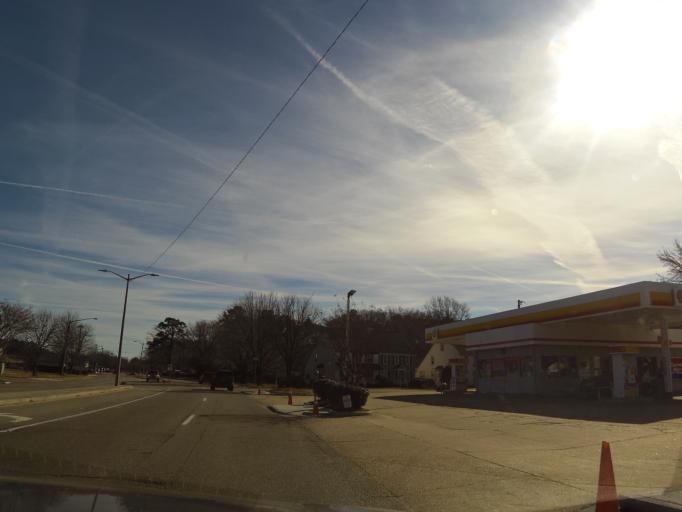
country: US
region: Virginia
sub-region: City of Newport News
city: Newport News
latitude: 37.0426
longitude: -76.4726
